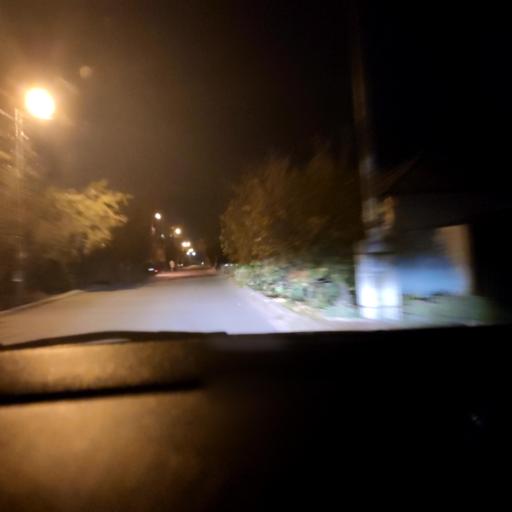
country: RU
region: Voronezj
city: Voronezh
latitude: 51.6371
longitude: 39.1642
